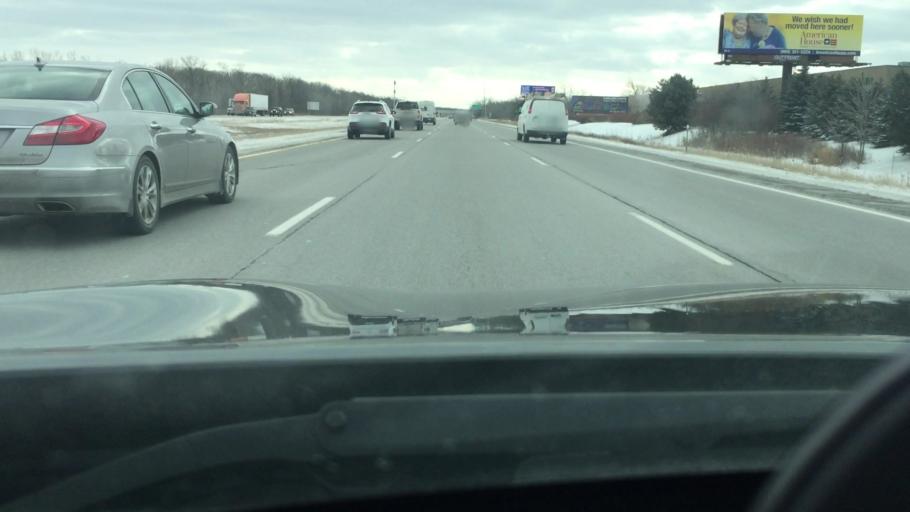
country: US
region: Michigan
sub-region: Wayne County
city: Romulus
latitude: 42.2594
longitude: -83.4408
